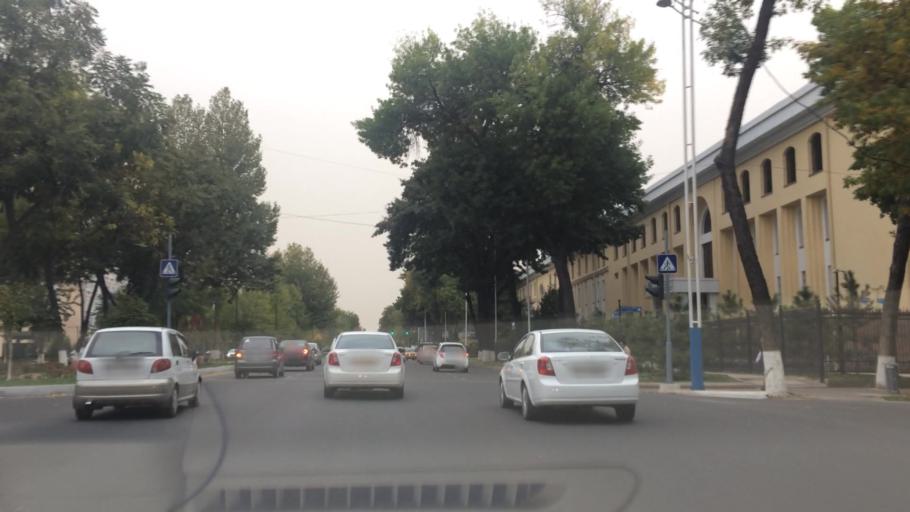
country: UZ
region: Toshkent Shahri
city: Tashkent
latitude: 41.3086
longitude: 69.2892
